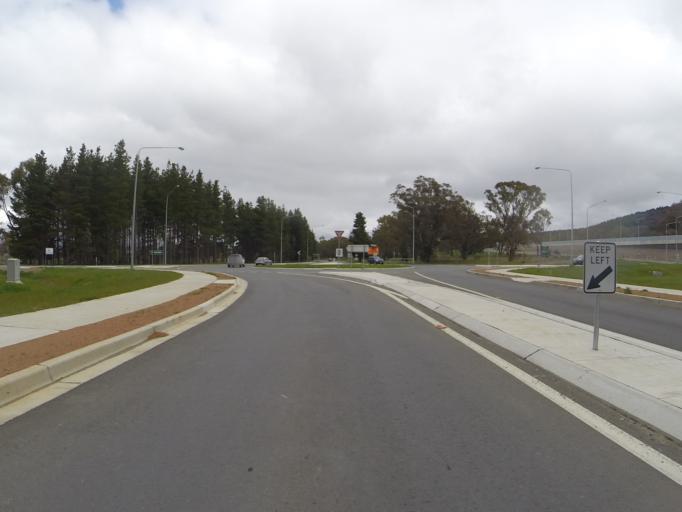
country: AU
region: Australian Capital Territory
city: Canberra
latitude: -35.2435
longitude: 149.1931
